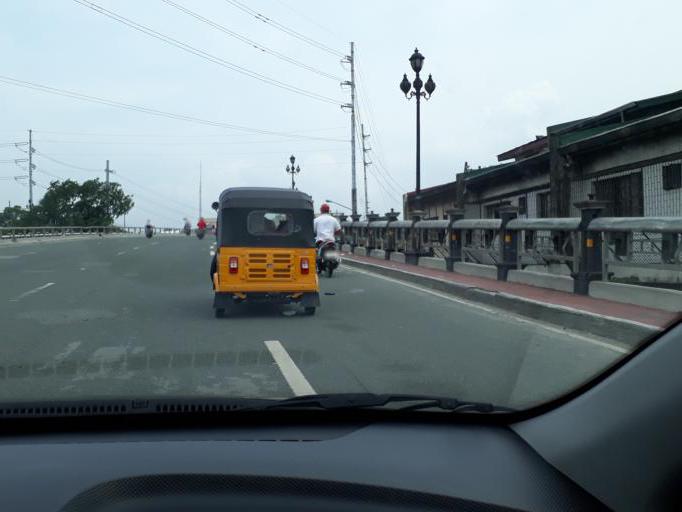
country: PH
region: Metro Manila
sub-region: City of Manila
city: Quiapo
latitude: 14.5981
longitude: 121.0010
